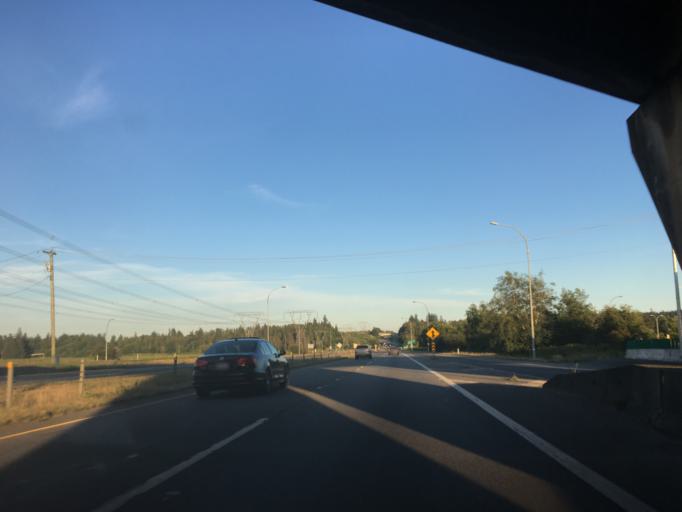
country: CA
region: British Columbia
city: Surrey
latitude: 49.0742
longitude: -122.8229
